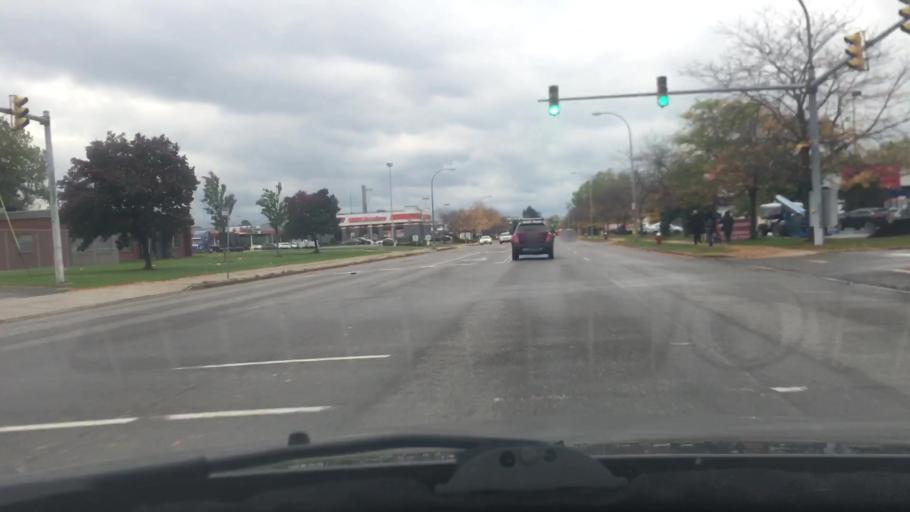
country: US
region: New York
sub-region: Erie County
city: Kenmore
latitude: 42.9536
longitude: -78.8784
